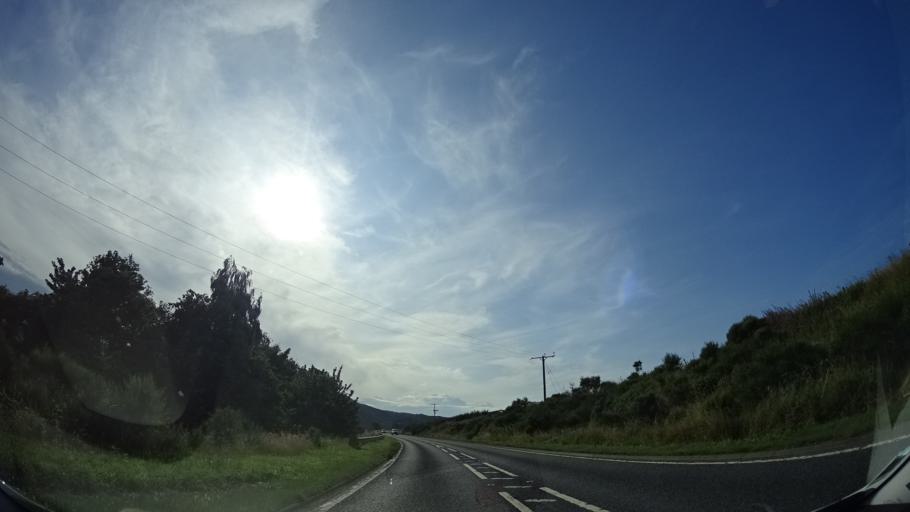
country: GB
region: Scotland
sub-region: Highland
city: Muir of Ord
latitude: 57.5609
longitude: -4.5551
